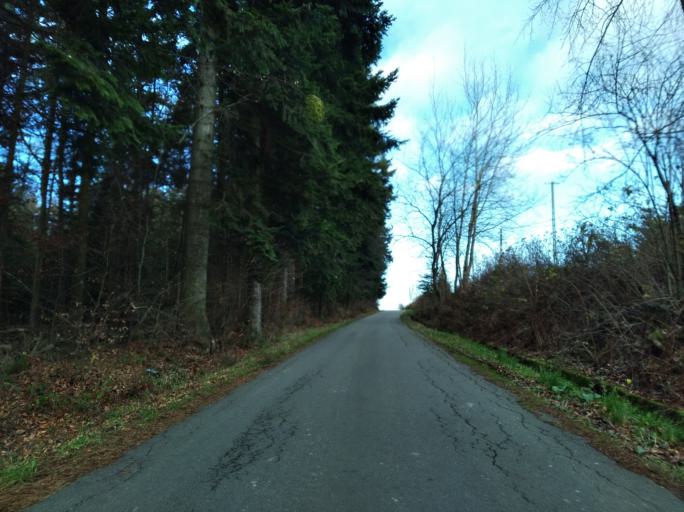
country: PL
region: Subcarpathian Voivodeship
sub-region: Powiat strzyzowski
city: Babica
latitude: 49.9090
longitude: 21.8494
